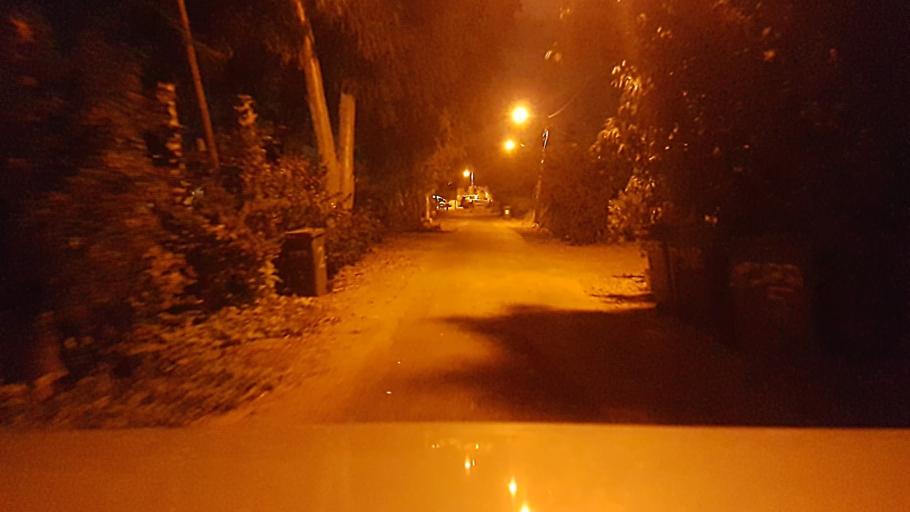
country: IL
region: Central District
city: Nehalim
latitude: 32.0772
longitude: 34.9199
